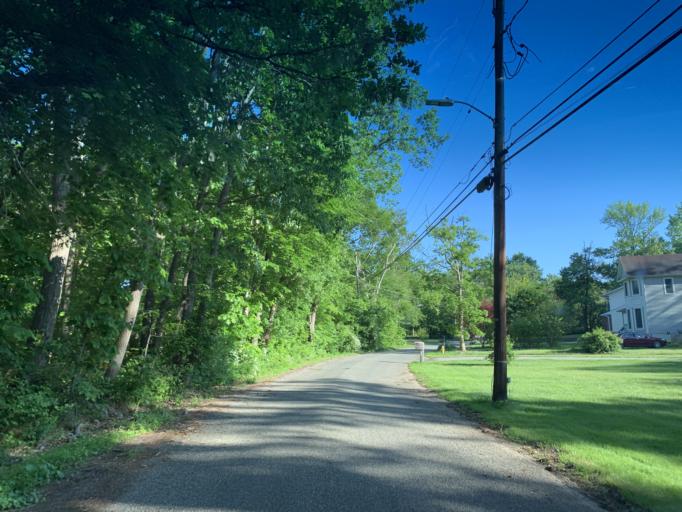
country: US
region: Maryland
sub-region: Harford County
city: Riverside
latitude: 39.4653
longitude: -76.2637
